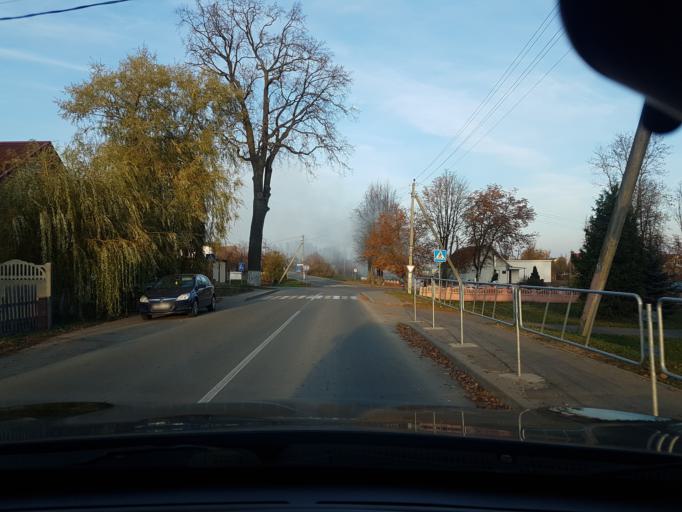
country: BY
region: Minsk
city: Shchomyslitsa
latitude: 53.8246
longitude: 27.4494
